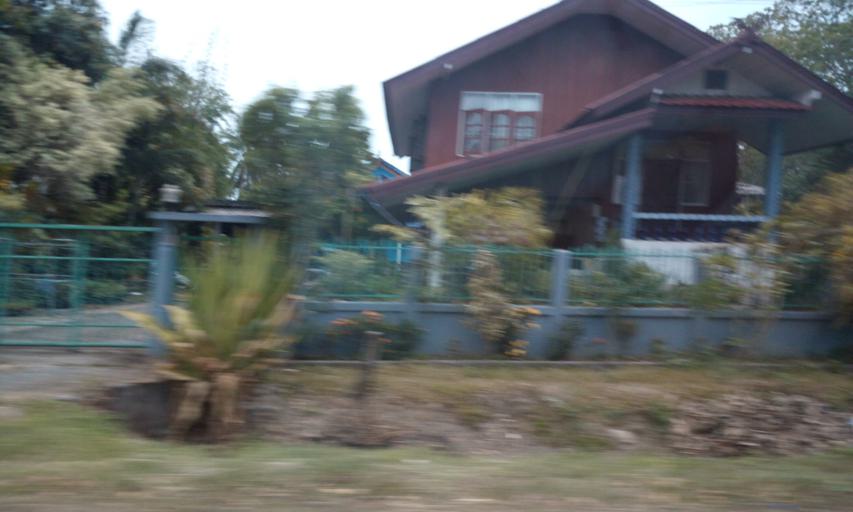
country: TH
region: Phayao
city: Chiang Kham
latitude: 19.5151
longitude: 100.3147
